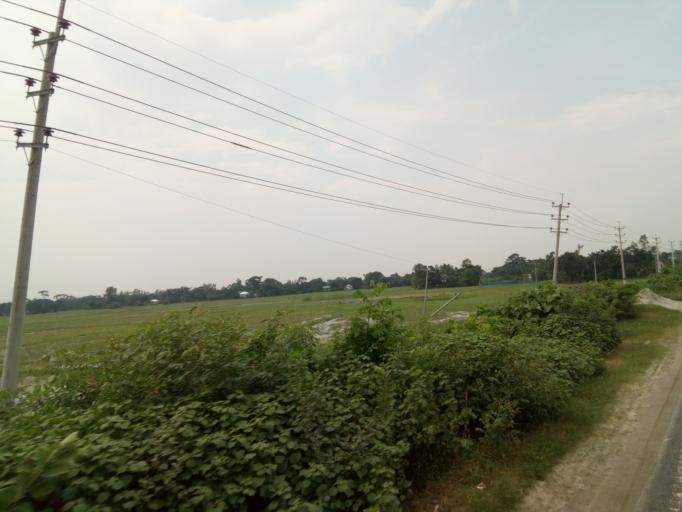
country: BD
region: Dhaka
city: Dohar
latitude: 23.5081
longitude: 90.2755
